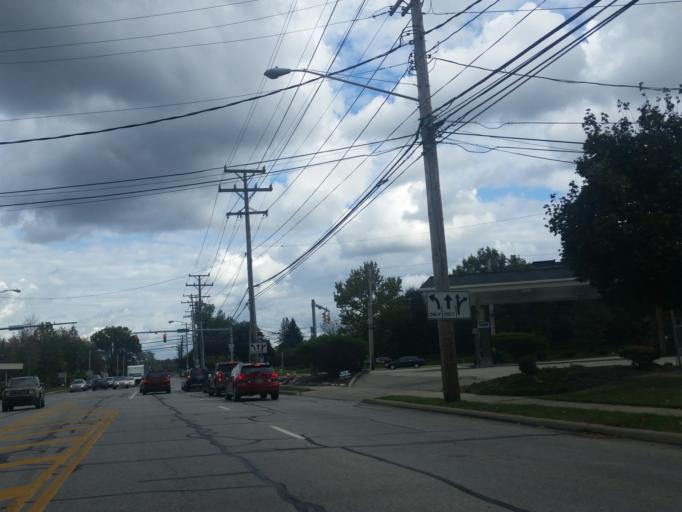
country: US
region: Ohio
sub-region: Cuyahoga County
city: Westlake
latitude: 41.4557
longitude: -81.9032
